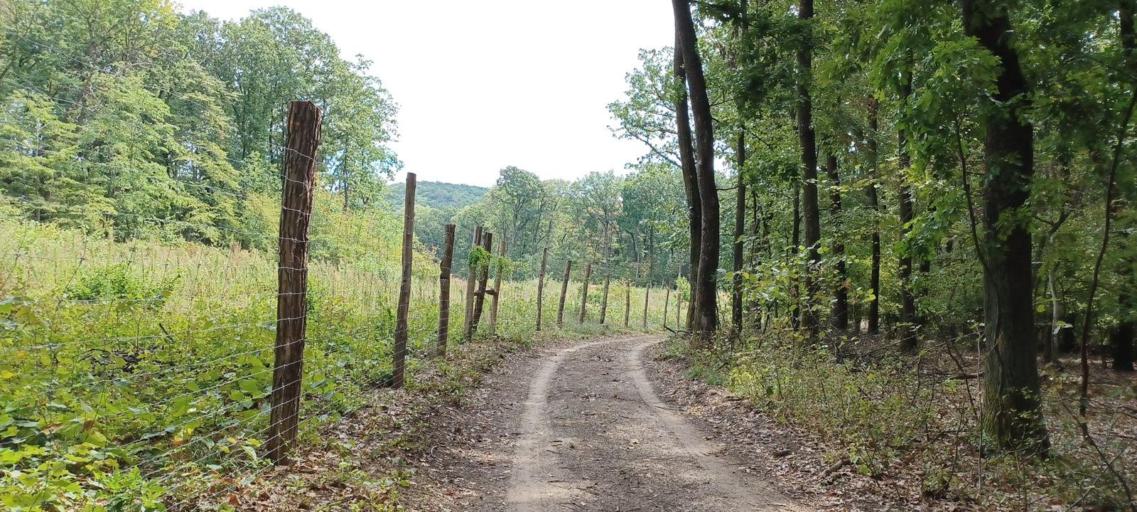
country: HU
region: Tolna
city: Szentgalpuszta
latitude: 46.3323
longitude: 18.6272
